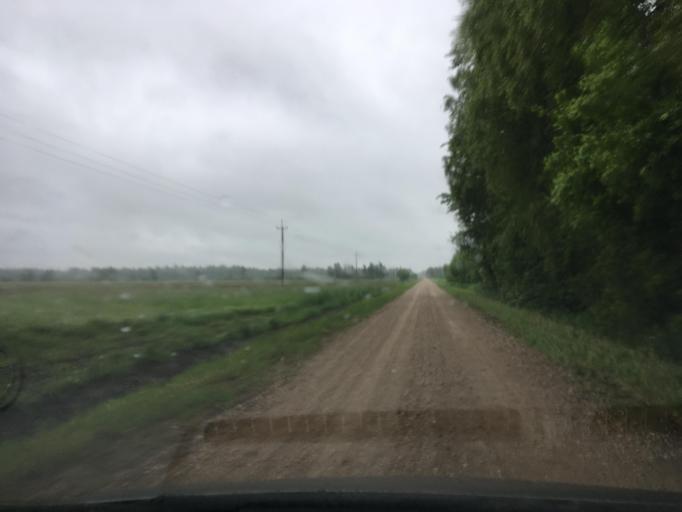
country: EE
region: Laeaene
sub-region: Lihula vald
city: Lihula
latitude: 58.6069
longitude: 23.8296
